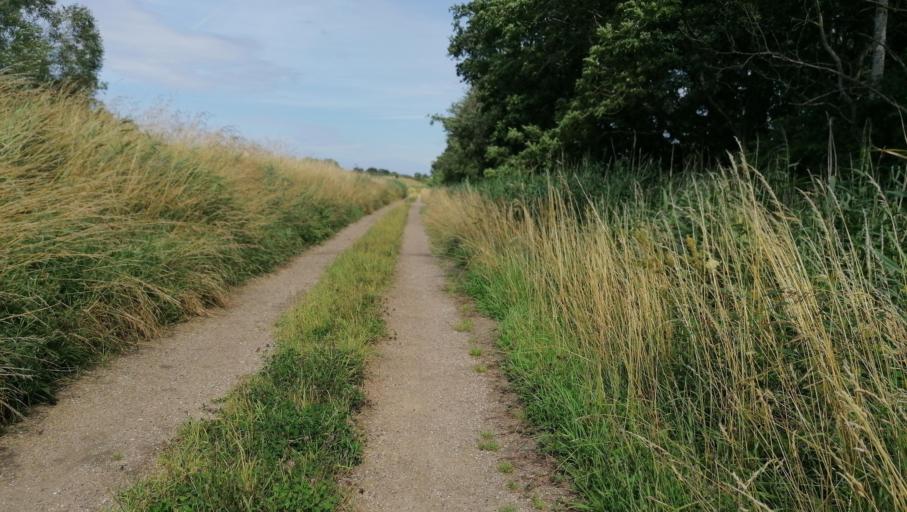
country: DK
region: Zealand
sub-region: Odsherred Kommune
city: Horve
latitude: 55.7869
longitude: 11.4218
